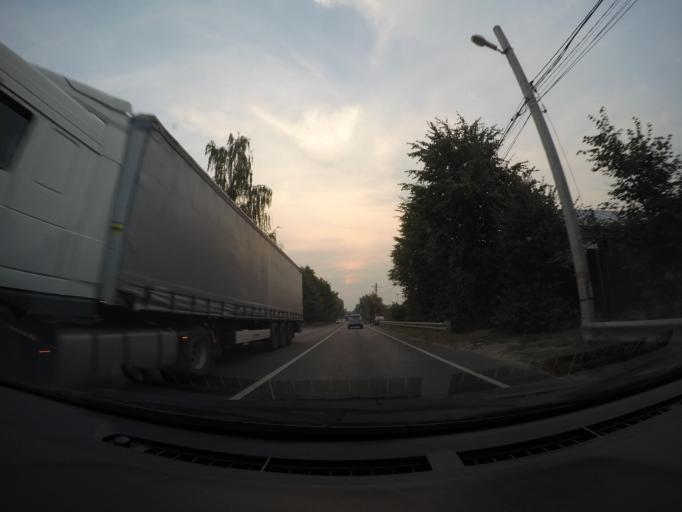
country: RU
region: Moskovskaya
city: Rechitsy
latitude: 55.5809
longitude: 38.5622
